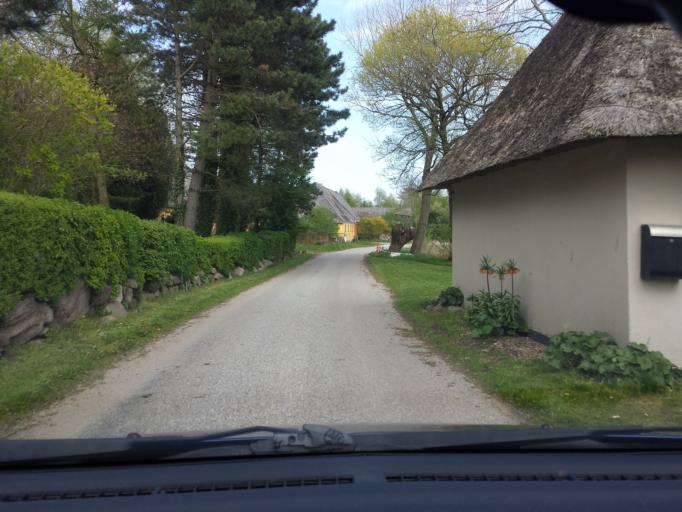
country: DK
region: South Denmark
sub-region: Langeland Kommune
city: Rudkobing
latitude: 54.8076
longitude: 10.6914
